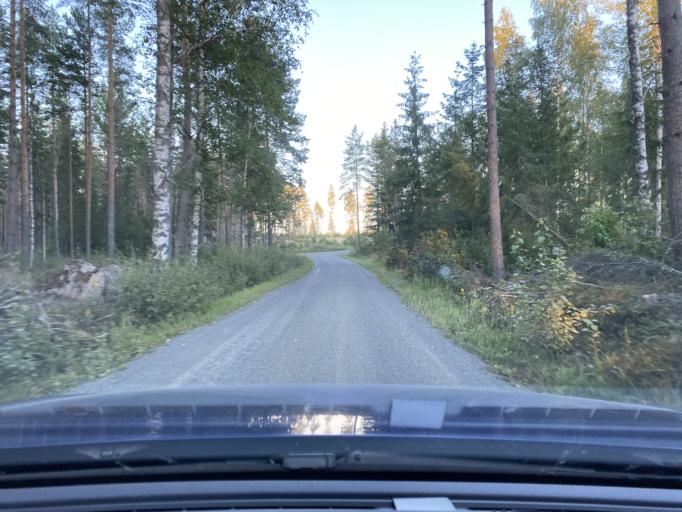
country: FI
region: Satakunta
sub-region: Rauma
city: Kiukainen
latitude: 61.1457
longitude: 22.0196
